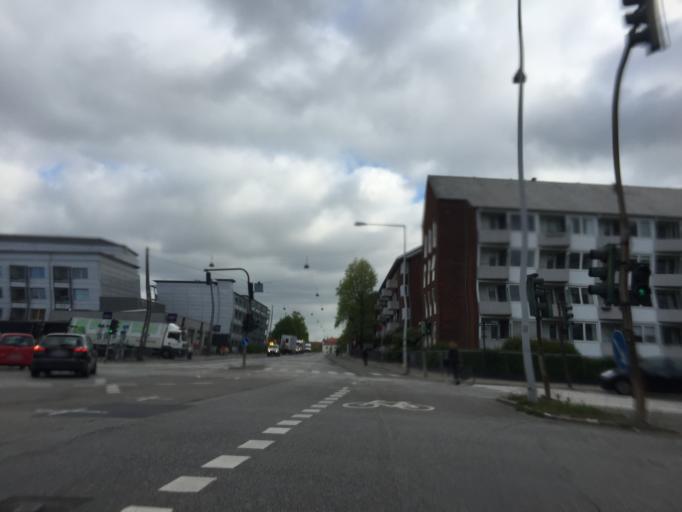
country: DK
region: Capital Region
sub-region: Frederiksberg Kommune
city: Frederiksberg
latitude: 55.7072
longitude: 12.5147
